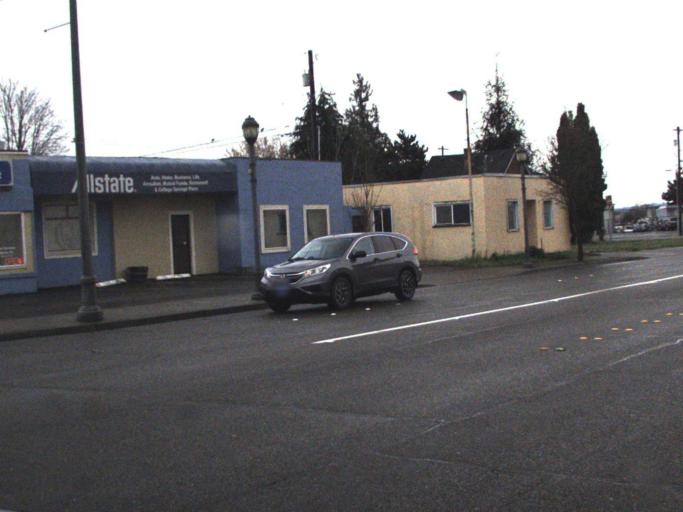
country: US
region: Washington
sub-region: Snohomish County
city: Marysville
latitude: 48.0497
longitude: -122.1770
